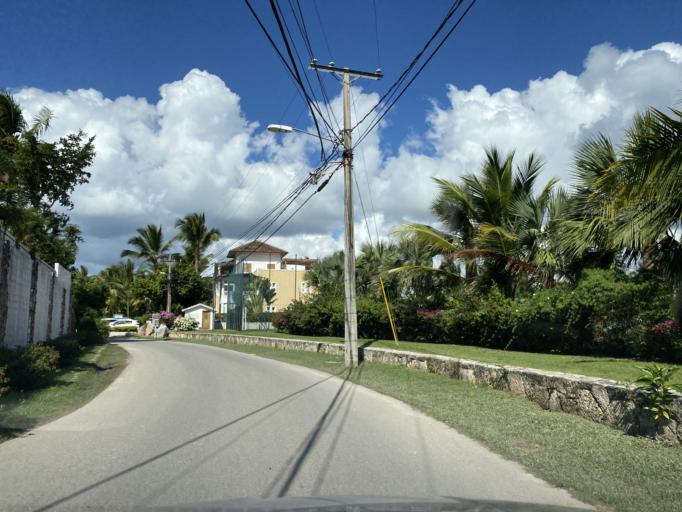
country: DO
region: La Romana
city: La Romana
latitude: 18.3505
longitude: -68.8322
